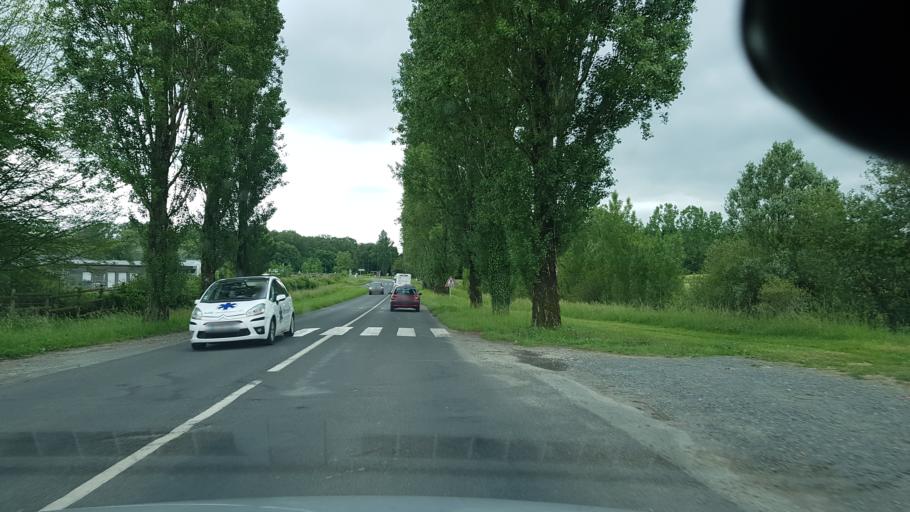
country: FR
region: Centre
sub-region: Departement d'Indre-et-Loire
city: Amboise
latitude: 47.3945
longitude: 0.9794
